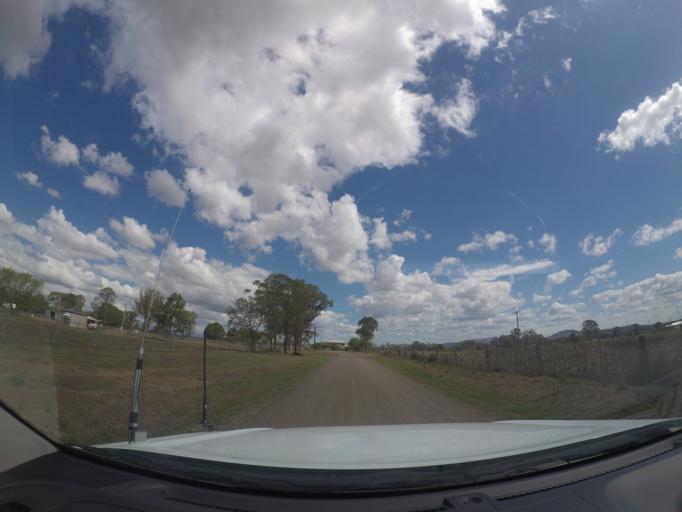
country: AU
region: Queensland
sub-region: Logan
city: Cedar Vale
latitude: -27.8963
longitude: 152.9585
